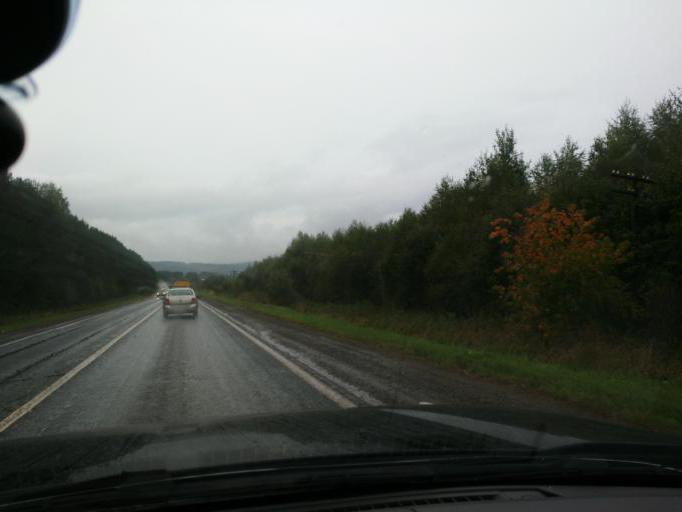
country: RU
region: Perm
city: Yugo-Kamskiy
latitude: 57.6781
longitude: 55.5774
